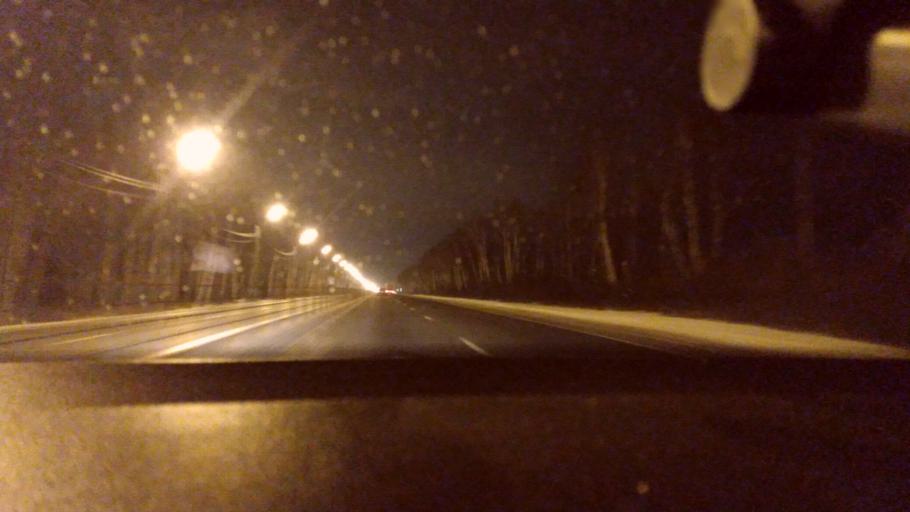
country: RU
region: Moskovskaya
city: Troitskoye
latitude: 55.2852
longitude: 38.4848
